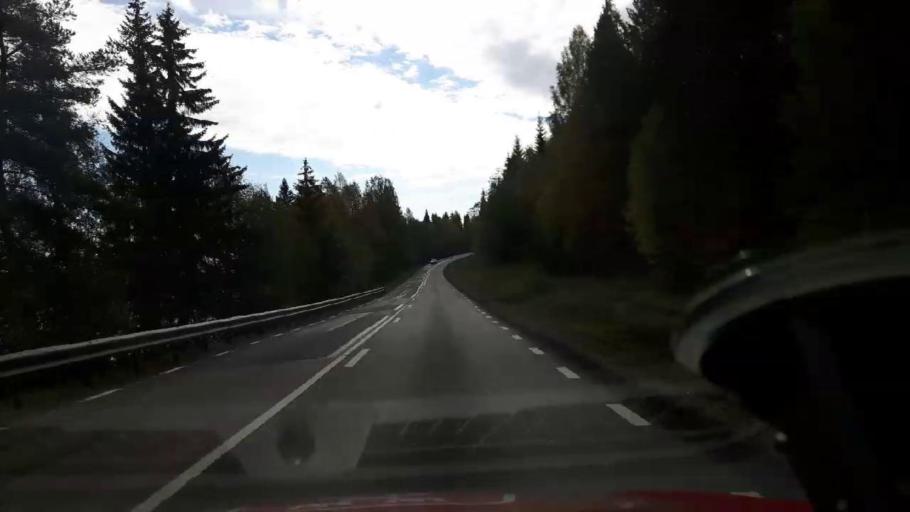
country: SE
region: Gaevleborg
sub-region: Ljusdals Kommun
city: Farila
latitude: 61.9561
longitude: 15.3613
